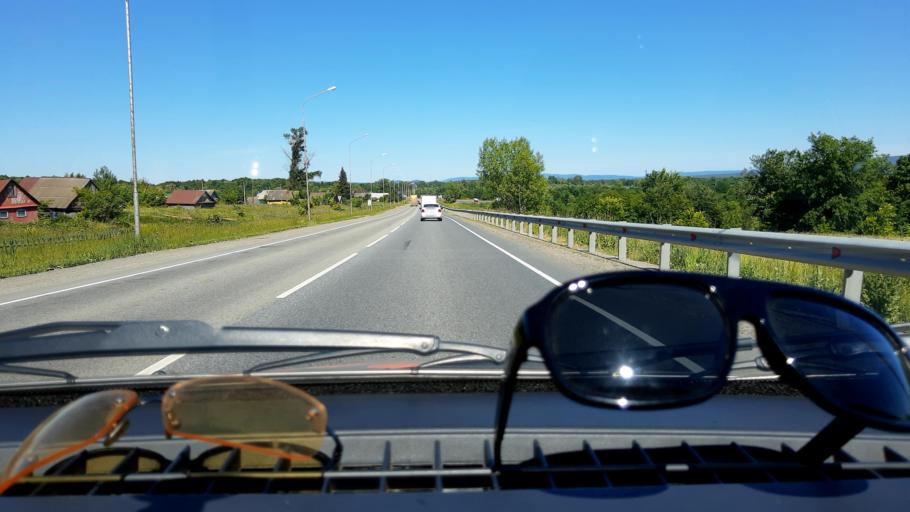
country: RU
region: Bashkortostan
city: Urman
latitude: 54.8208
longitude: 56.8818
